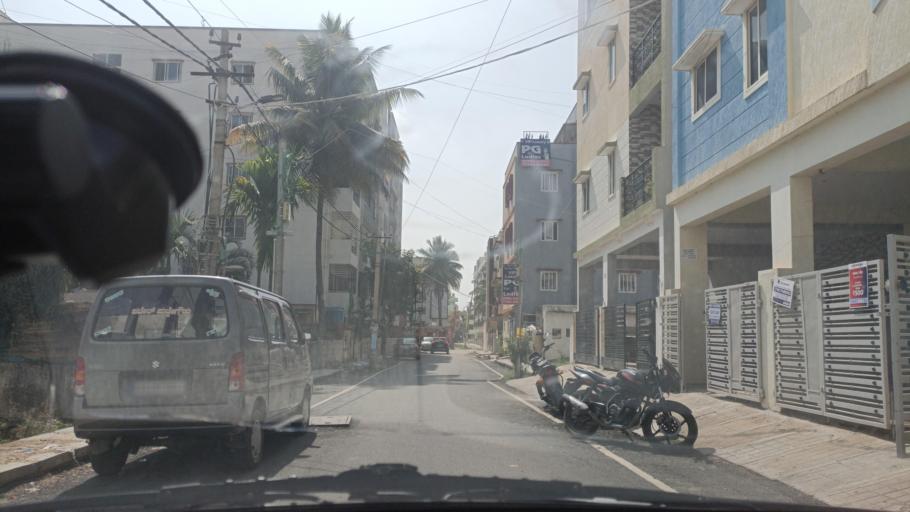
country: IN
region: Karnataka
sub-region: Bangalore Urban
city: Yelahanka
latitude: 13.1202
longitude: 77.6151
